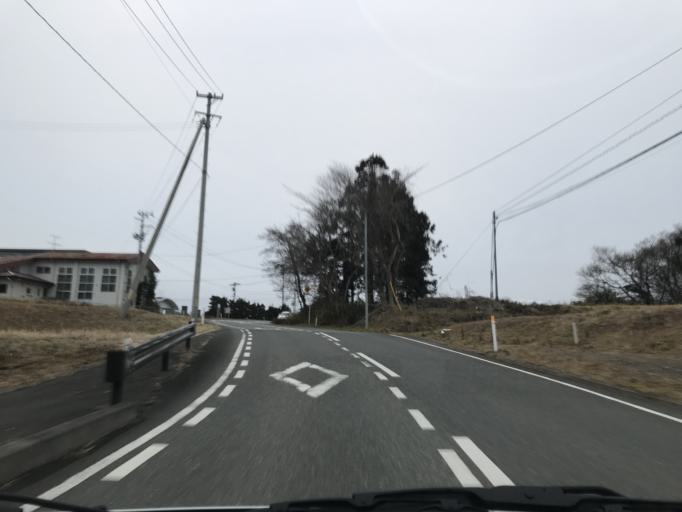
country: JP
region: Miyagi
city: Kogota
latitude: 38.6809
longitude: 141.0973
